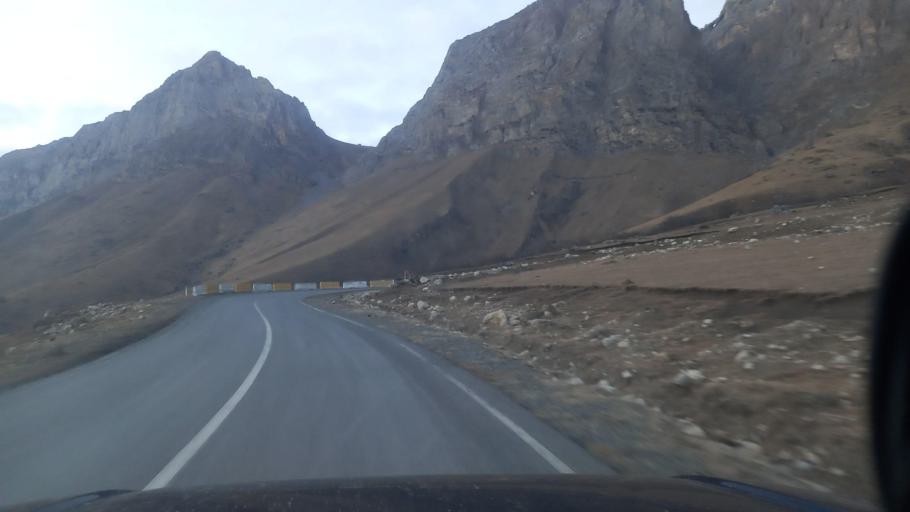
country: RU
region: Ingushetiya
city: Dzhayrakh
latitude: 42.8244
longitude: 44.8244
